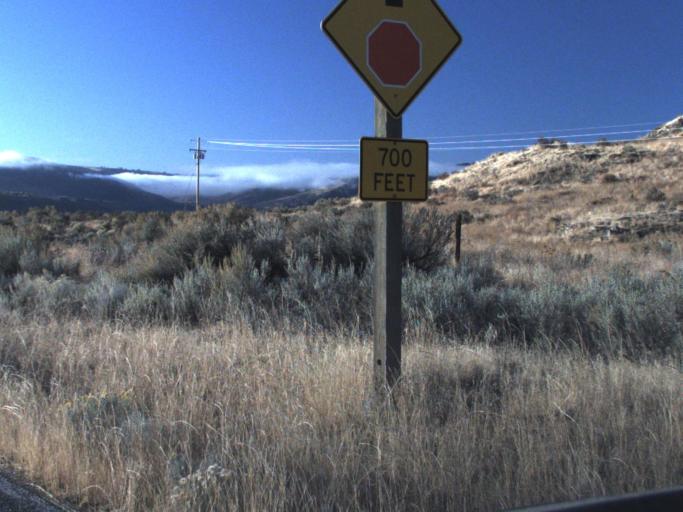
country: US
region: Washington
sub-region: Okanogan County
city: Coulee Dam
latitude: 47.9485
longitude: -118.6899
